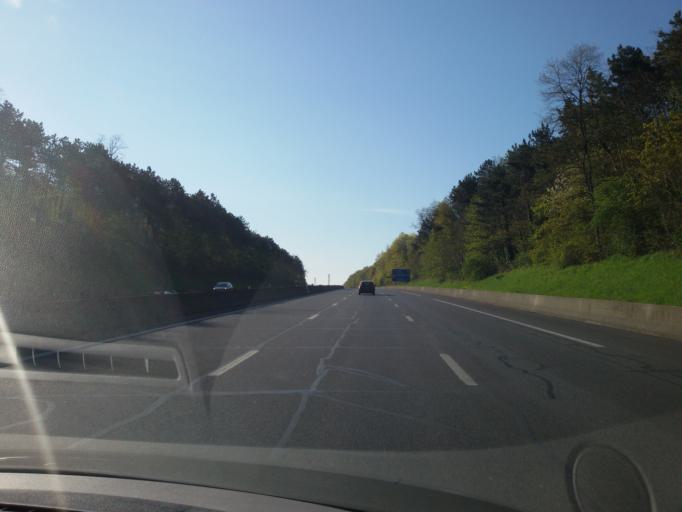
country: FR
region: Ile-de-France
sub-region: Departement de Seine-et-Marne
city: Bagneaux-sur-Loing
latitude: 48.2551
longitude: 2.7297
